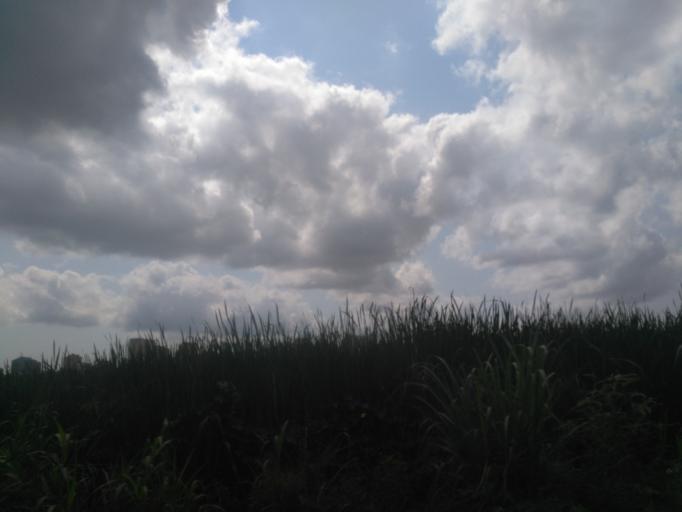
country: TZ
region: Dar es Salaam
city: Dar es Salaam
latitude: -6.8134
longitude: 39.2666
